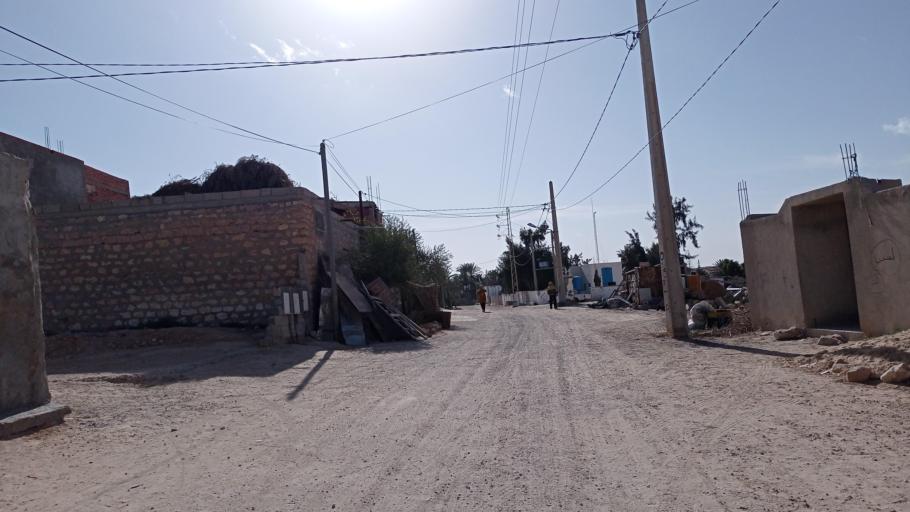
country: TN
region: Qabis
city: Gabes
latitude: 33.8316
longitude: 10.1116
